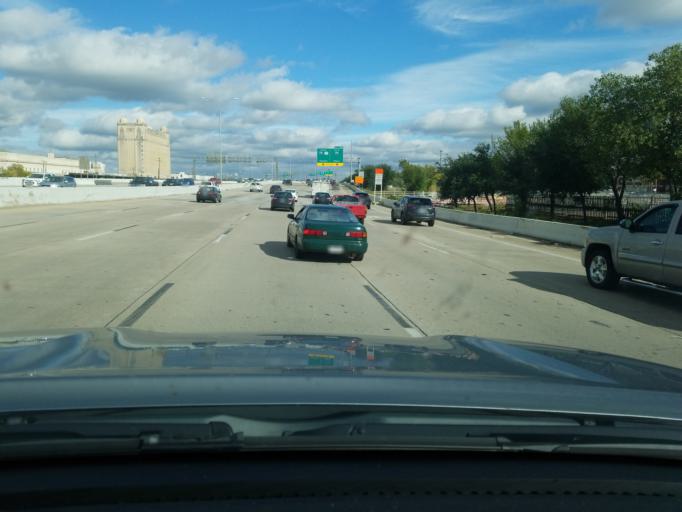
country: US
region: Texas
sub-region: Tarrant County
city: Fort Worth
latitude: 32.7447
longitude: -97.3328
